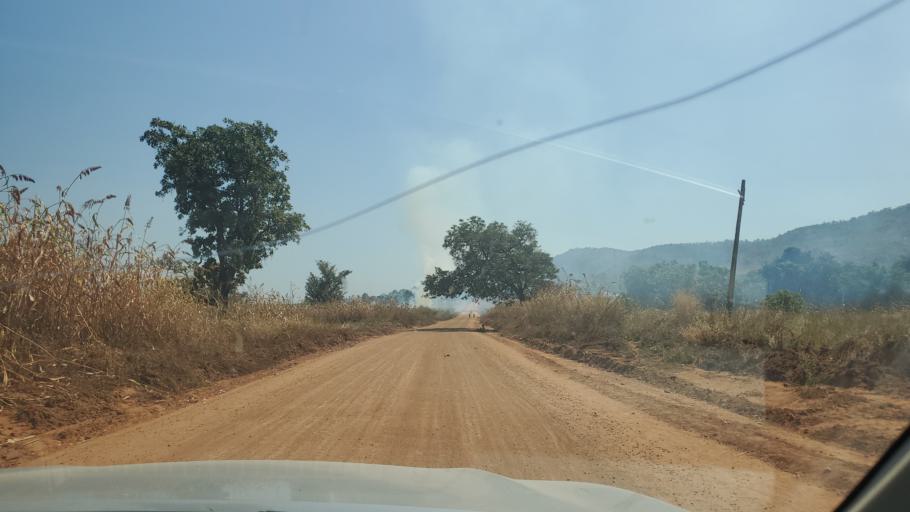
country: NG
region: Niger
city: Gawu Babangida
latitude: 9.2191
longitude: 6.8416
